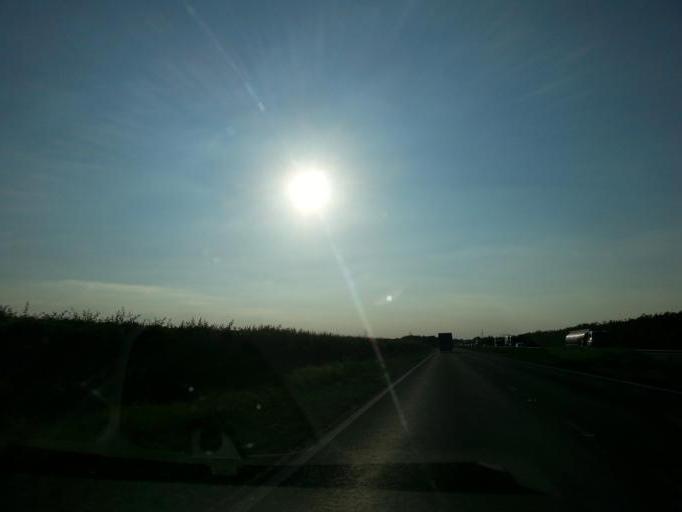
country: GB
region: England
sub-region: Lincolnshire
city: Long Bennington
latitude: 52.9767
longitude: -0.7371
